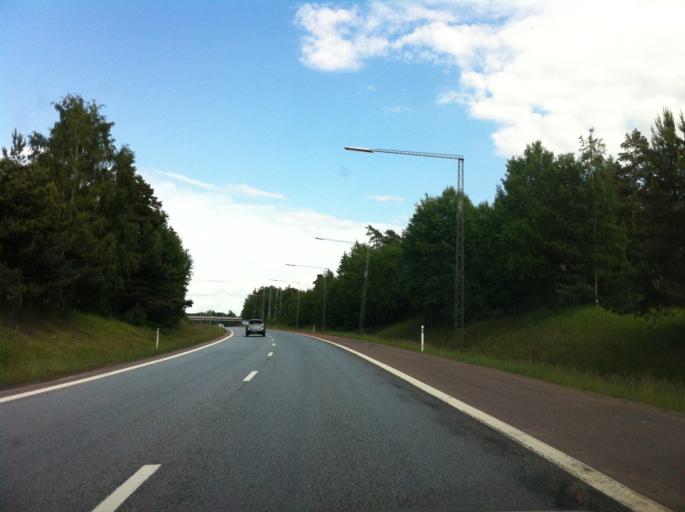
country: SE
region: Vaermland
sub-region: Hammaro Kommun
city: Skoghall
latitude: 59.3820
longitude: 13.4104
